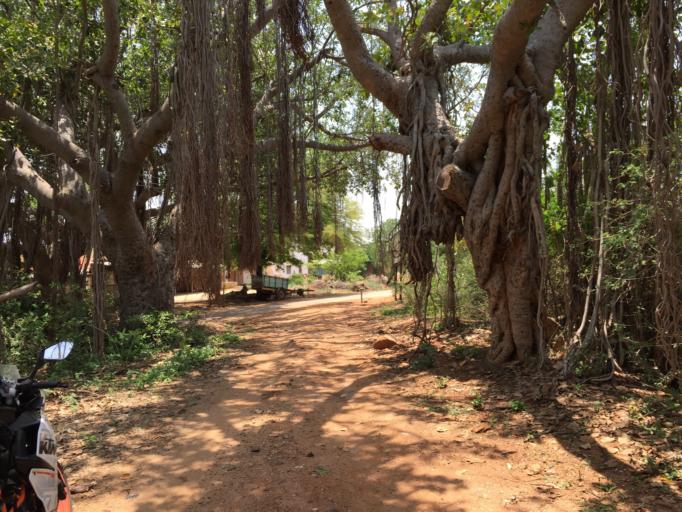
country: IN
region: Karnataka
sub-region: Mandya
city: Malavalli
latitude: 12.4075
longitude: 77.2274
